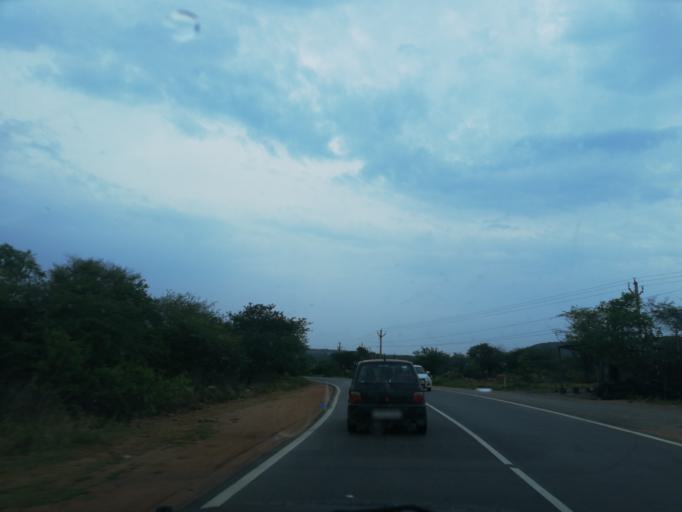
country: IN
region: Andhra Pradesh
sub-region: Guntur
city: Macherla
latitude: 16.6356
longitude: 79.2892
